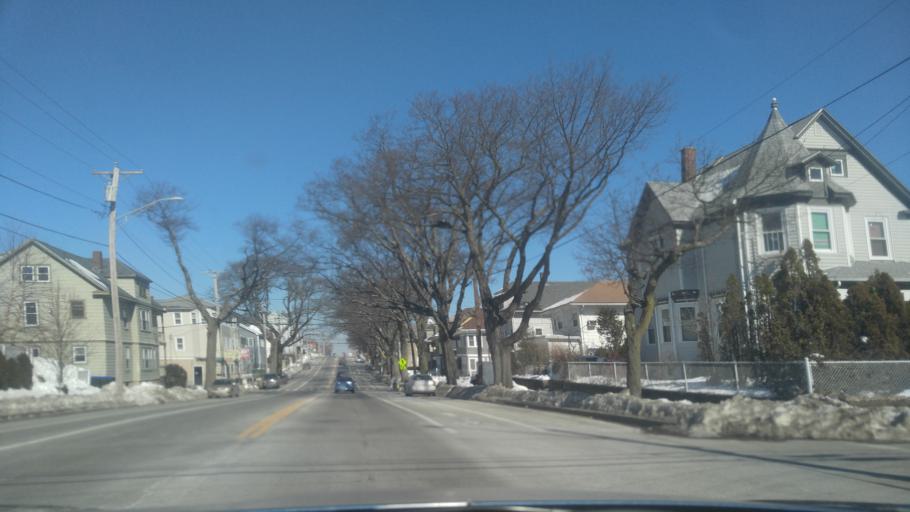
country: US
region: Rhode Island
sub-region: Providence County
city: East Providence
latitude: 41.7882
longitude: -71.3956
